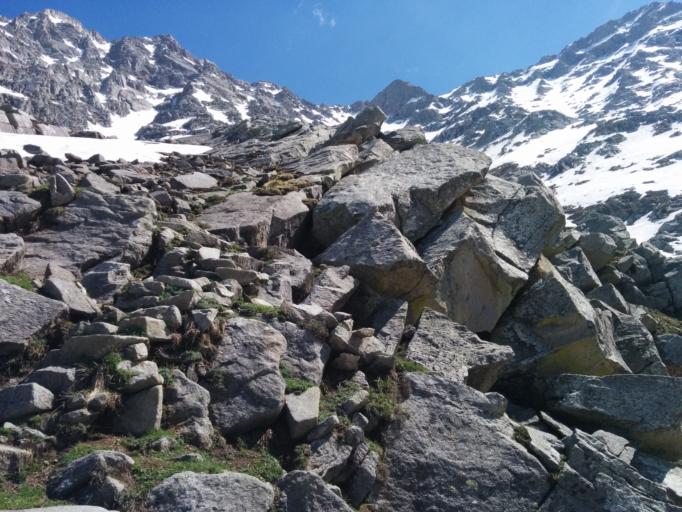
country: IN
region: Himachal Pradesh
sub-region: Kangra
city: Dharmsala
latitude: 32.2879
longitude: 76.3725
